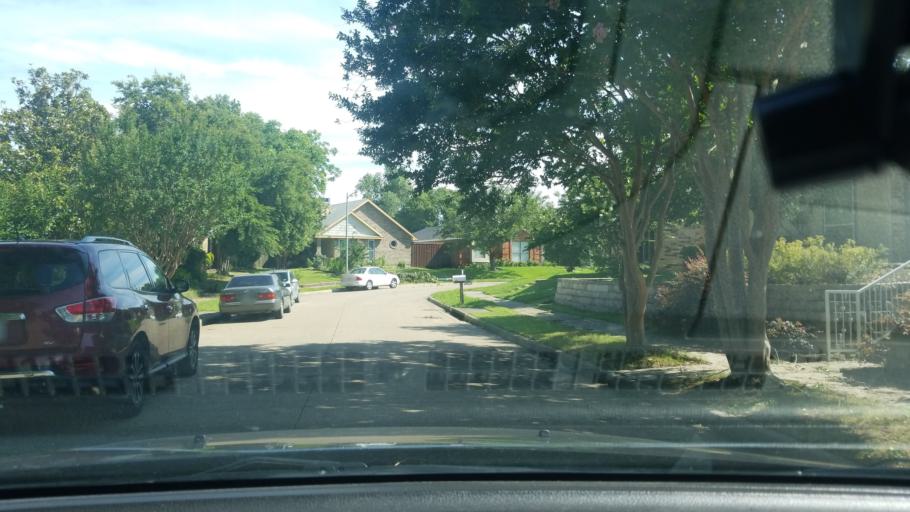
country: US
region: Texas
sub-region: Dallas County
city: Mesquite
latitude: 32.7770
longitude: -96.5959
